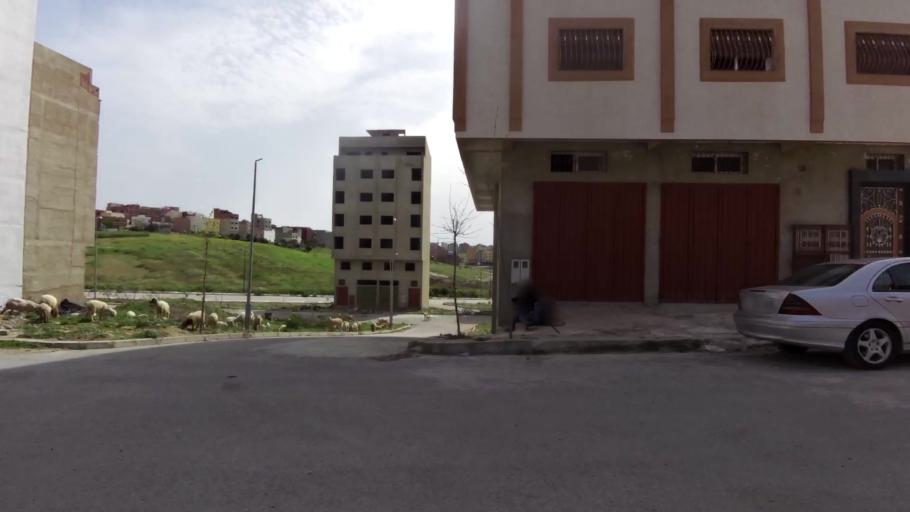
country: MA
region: Tanger-Tetouan
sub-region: Tanger-Assilah
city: Tangier
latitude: 35.7390
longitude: -5.8380
